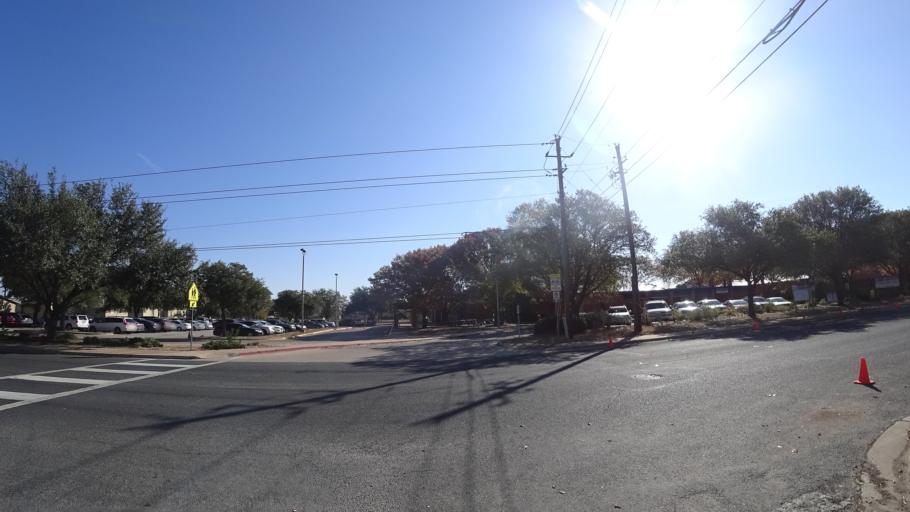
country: US
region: Texas
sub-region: Travis County
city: Barton Creek
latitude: 30.2327
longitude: -97.8460
